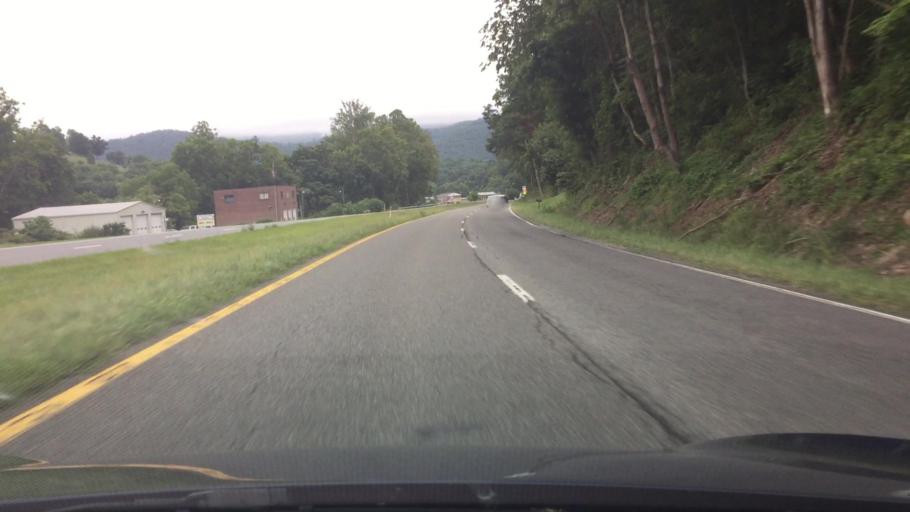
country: US
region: Virginia
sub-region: Montgomery County
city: Shawsville
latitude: 37.1709
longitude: -80.2652
